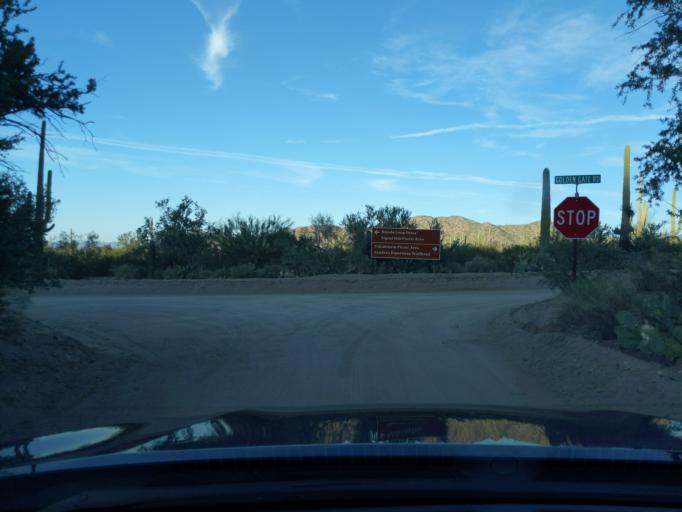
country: US
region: Arizona
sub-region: Pima County
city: Picture Rocks
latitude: 32.2856
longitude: -111.1874
